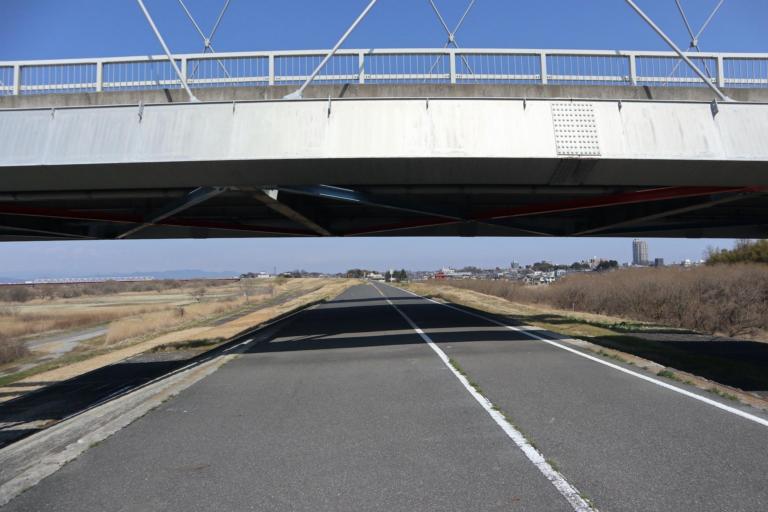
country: JP
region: Ibaraki
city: Koga
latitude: 36.1832
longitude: 139.6953
